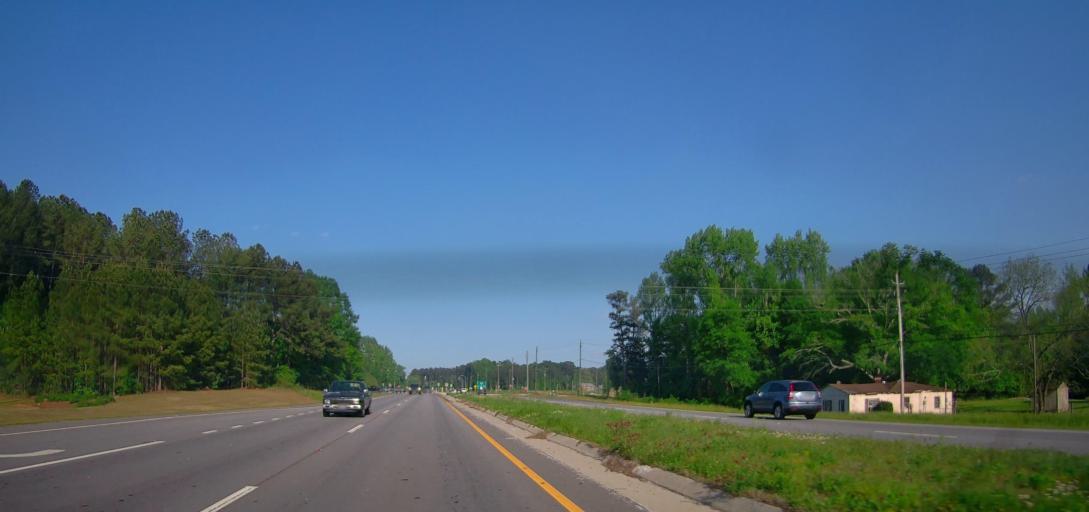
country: US
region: Georgia
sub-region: Newton County
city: Covington
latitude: 33.5928
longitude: -83.7982
